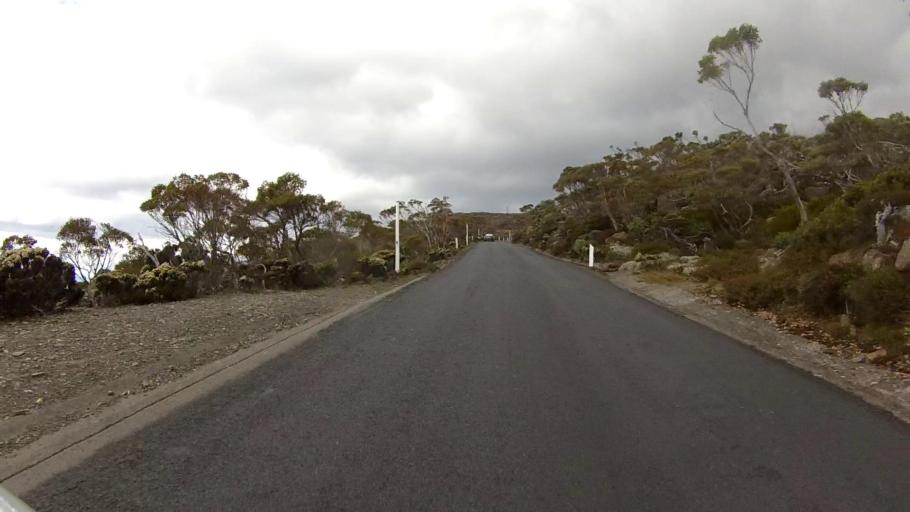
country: AU
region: Tasmania
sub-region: Glenorchy
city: West Moonah
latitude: -42.8903
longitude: 147.2219
